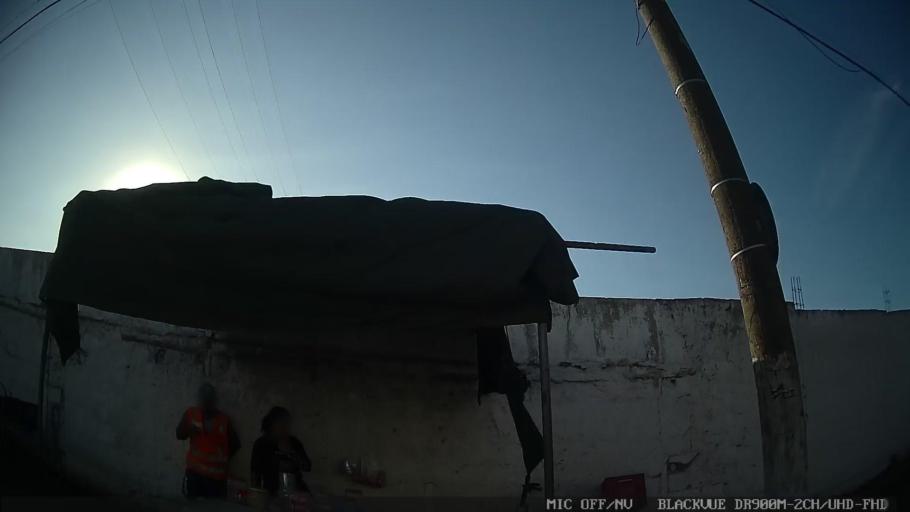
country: BR
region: Sao Paulo
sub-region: Guaruja
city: Guaruja
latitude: -23.9630
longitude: -46.2772
